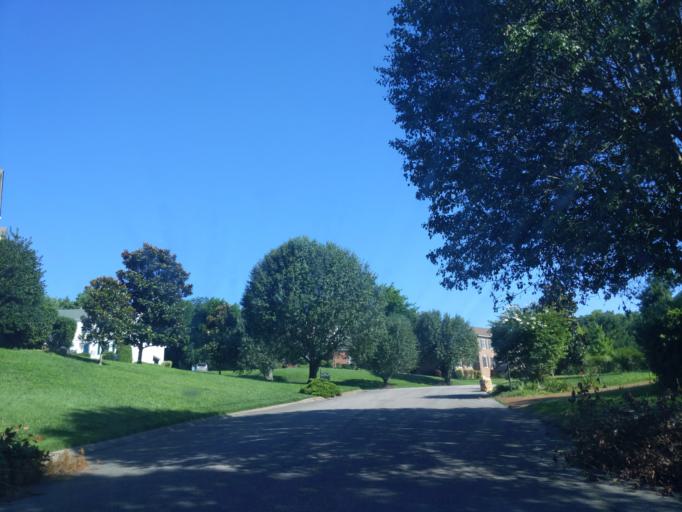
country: US
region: Tennessee
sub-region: Williamson County
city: Brentwood Estates
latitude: 36.0243
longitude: -86.7557
